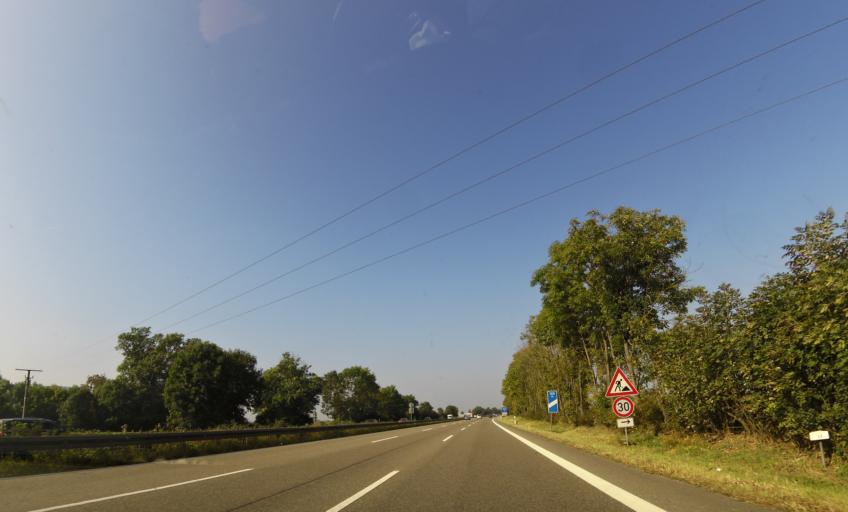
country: DE
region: Baden-Wuerttemberg
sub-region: Regierungsbezirk Stuttgart
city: Waldenburg
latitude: 49.2051
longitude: 9.6491
